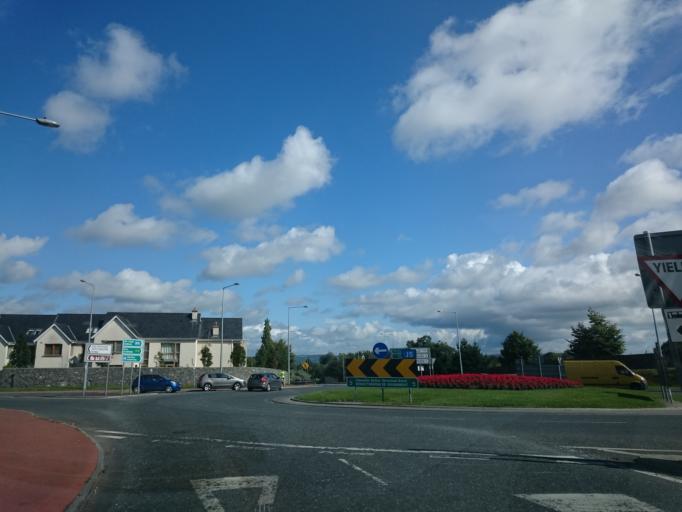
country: IE
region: Leinster
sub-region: Kilkenny
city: Kilkenny
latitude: 52.6417
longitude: -7.2316
